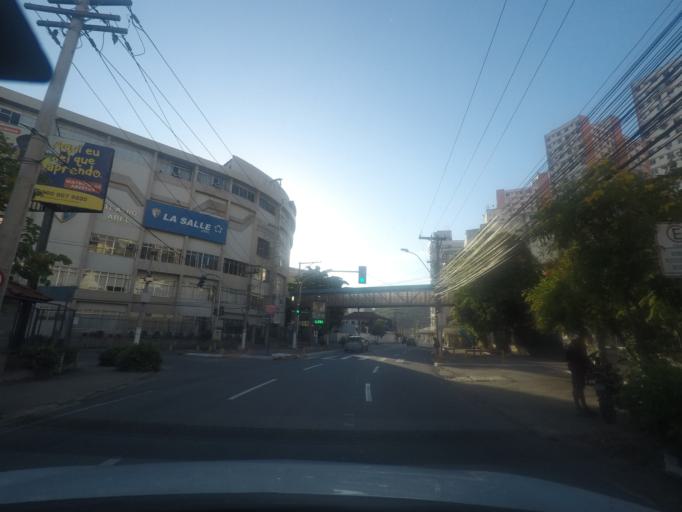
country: BR
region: Rio de Janeiro
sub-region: Niteroi
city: Niteroi
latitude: -22.8996
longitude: -43.1087
